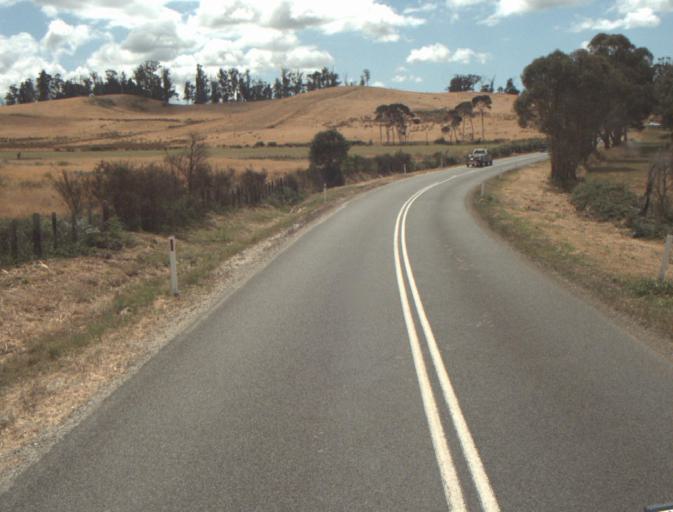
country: AU
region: Tasmania
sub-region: Launceston
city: Mayfield
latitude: -41.2242
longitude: 147.1221
